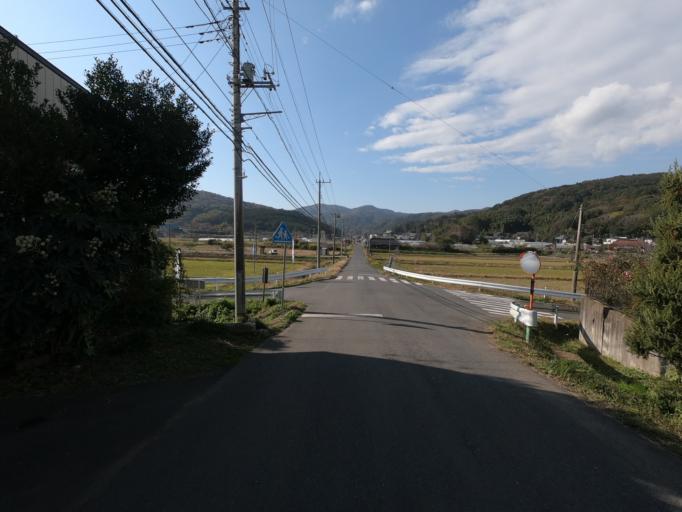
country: JP
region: Ibaraki
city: Tsukuba
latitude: 36.1878
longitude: 140.1740
